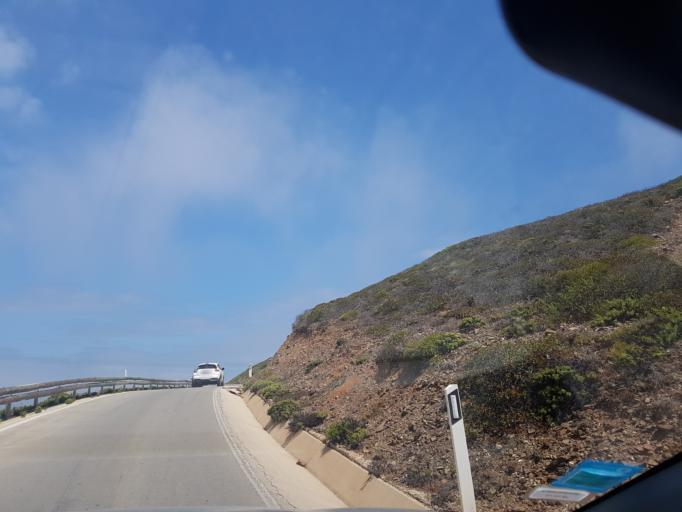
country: PT
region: Faro
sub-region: Vila do Bispo
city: Vila do Bispo
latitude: 37.1062
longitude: -8.9337
